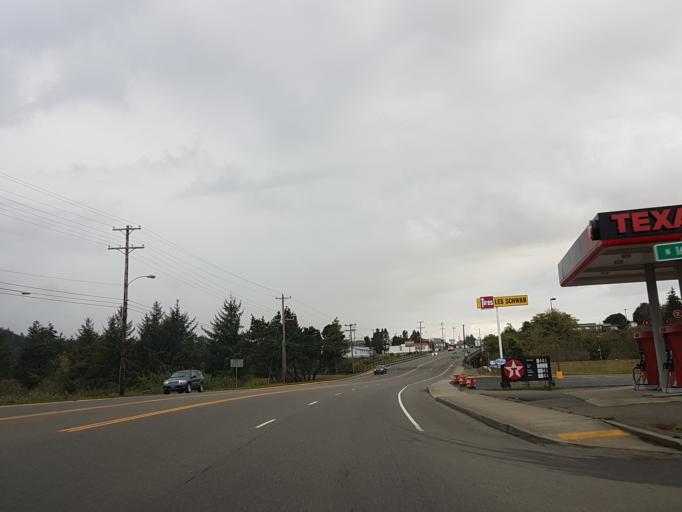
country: US
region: Oregon
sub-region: Douglas County
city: Reedsport
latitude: 43.6977
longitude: -124.1126
